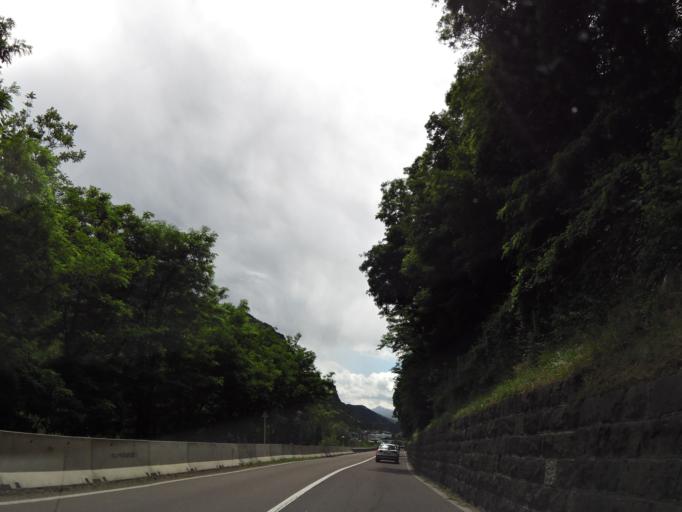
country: IT
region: Trentino-Alto Adige
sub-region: Bolzano
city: Ponte Gardena
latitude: 46.6026
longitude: 11.5321
